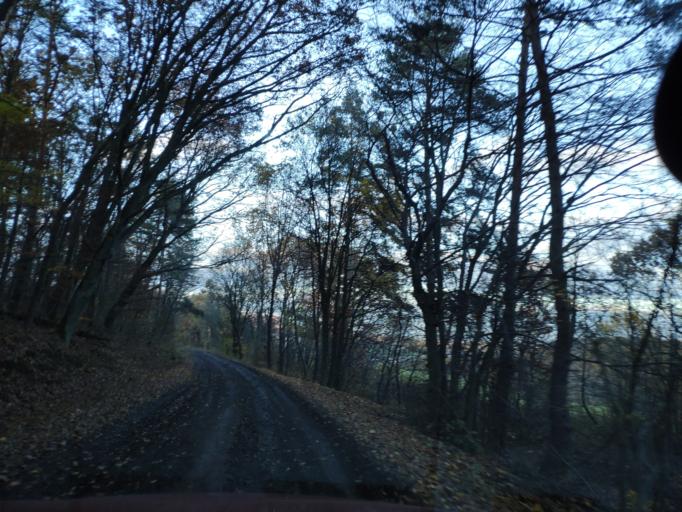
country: SK
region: Kosicky
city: Secovce
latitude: 48.6045
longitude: 21.5184
